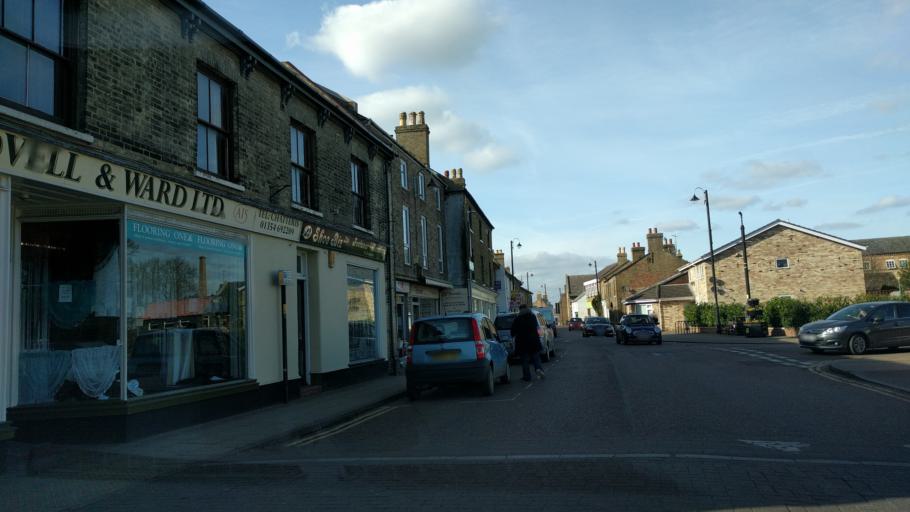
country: GB
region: England
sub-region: Cambridgeshire
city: Chatteris
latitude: 52.4562
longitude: 0.0489
